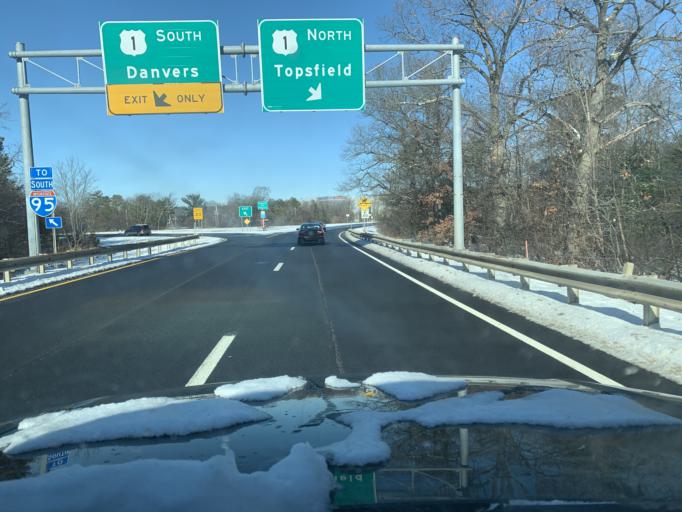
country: US
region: Massachusetts
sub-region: Essex County
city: Danvers
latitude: 42.5959
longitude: -70.9609
